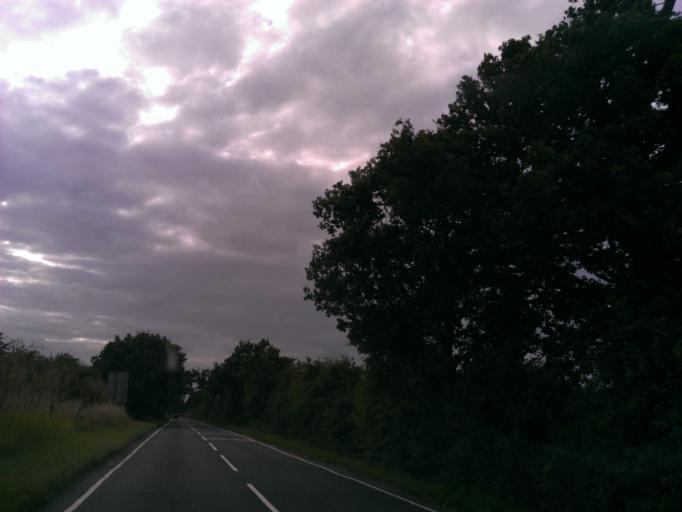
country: GB
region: England
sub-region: Essex
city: Wivenhoe
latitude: 51.8749
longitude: 0.9688
